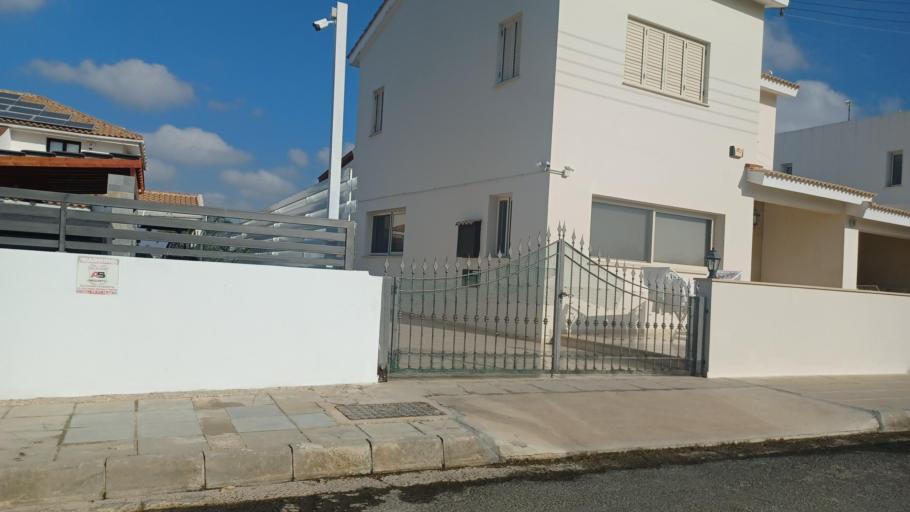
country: CY
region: Pafos
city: Mesogi
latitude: 34.7795
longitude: 32.4662
